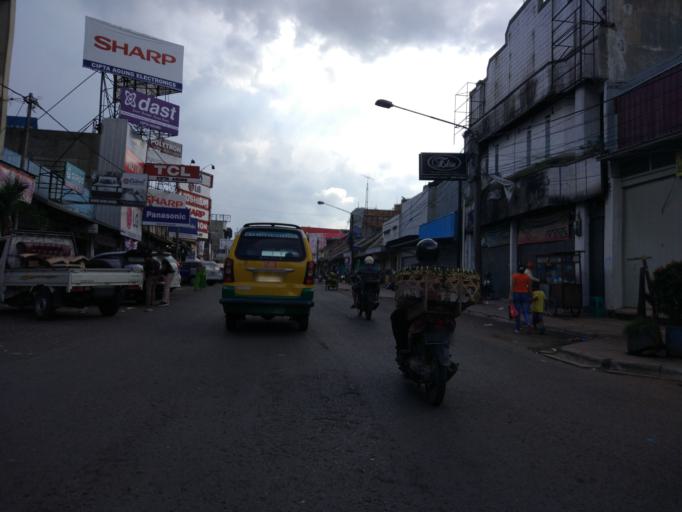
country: ID
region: West Java
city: Bandung
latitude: -6.9190
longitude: 107.5893
